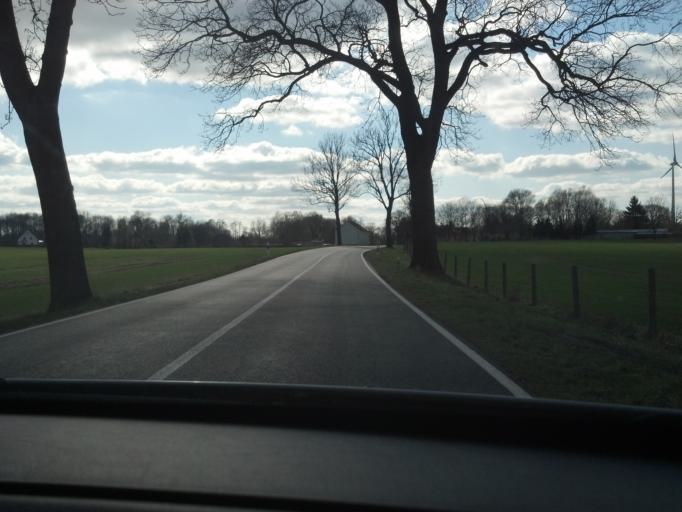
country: DE
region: Brandenburg
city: Gerdshagen
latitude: 53.2933
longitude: 12.1817
